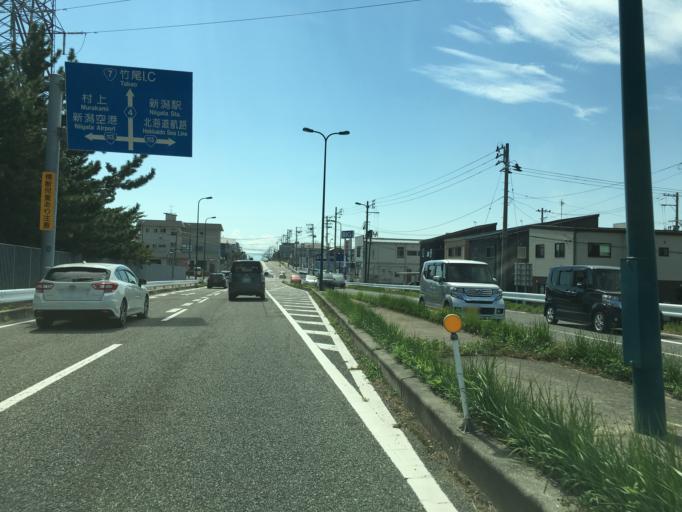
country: JP
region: Niigata
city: Niigata-shi
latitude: 37.9442
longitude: 139.0866
